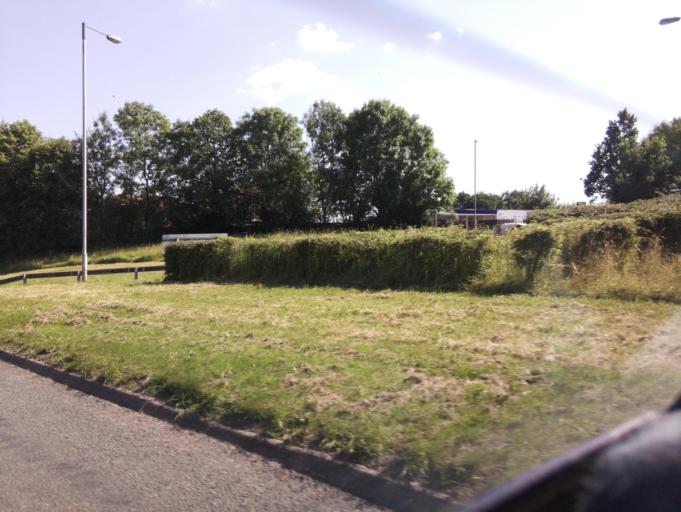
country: GB
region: England
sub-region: Worcestershire
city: Redditch
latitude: 52.3058
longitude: -1.9784
